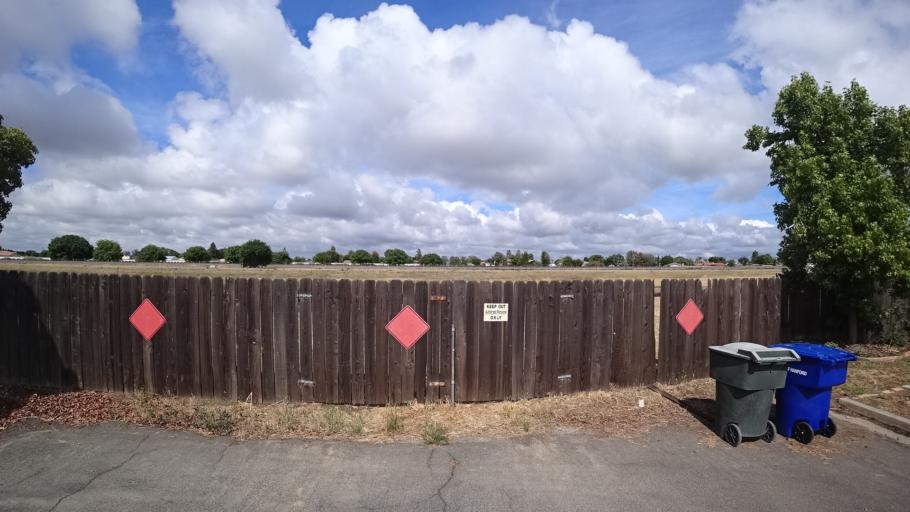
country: US
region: California
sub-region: Kings County
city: Hanford
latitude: 36.3455
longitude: -119.6619
